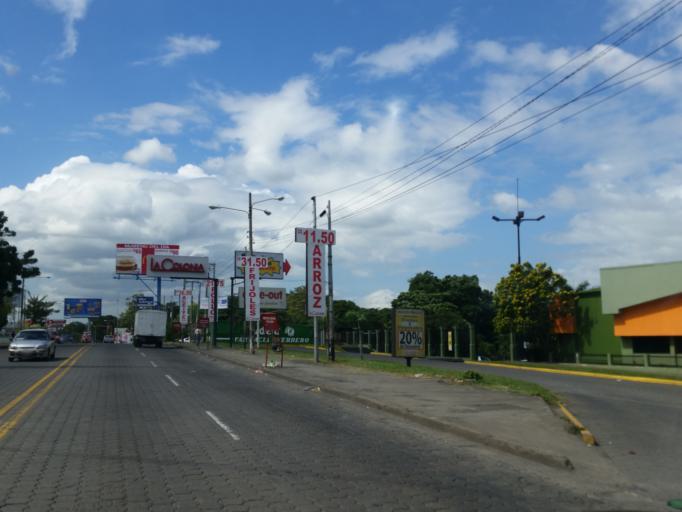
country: NI
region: Managua
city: Managua
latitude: 12.1320
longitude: -86.2592
